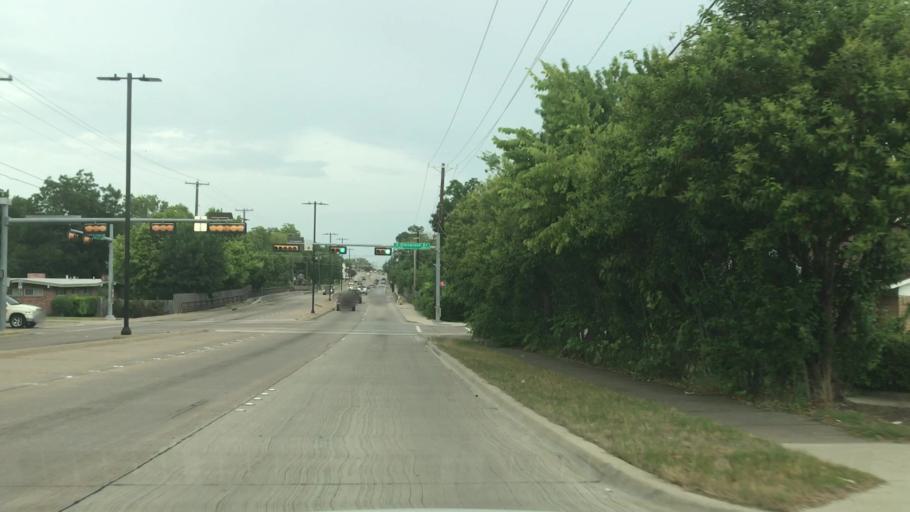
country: US
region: Texas
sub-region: Dallas County
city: Garland
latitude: 32.8787
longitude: -96.6392
